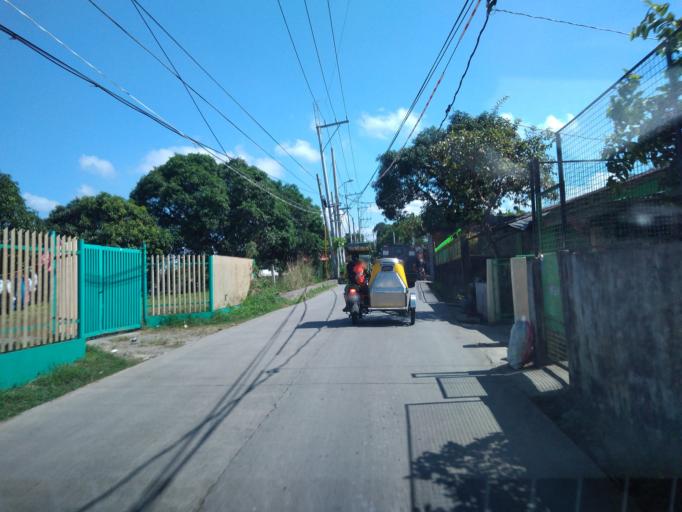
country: PH
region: Central Luzon
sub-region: Province of Bulacan
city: Balasing
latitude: 14.8526
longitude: 121.0094
